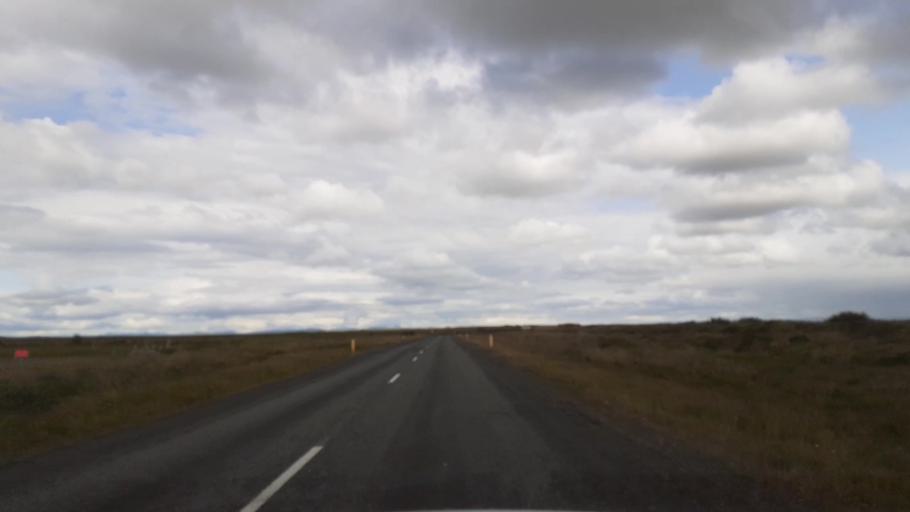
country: IS
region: South
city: Vestmannaeyjar
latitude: 63.8204
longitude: -20.4273
